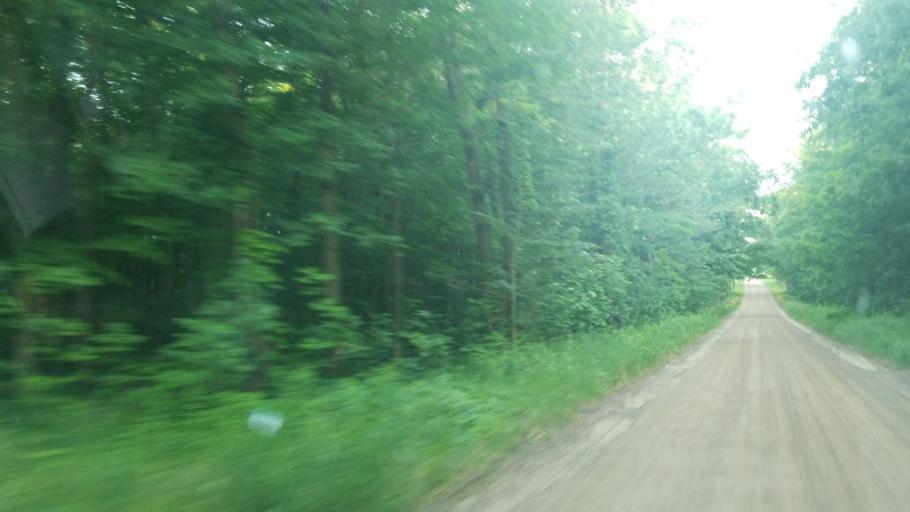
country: US
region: Michigan
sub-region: Barry County
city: Nashville
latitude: 42.5970
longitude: -84.9830
